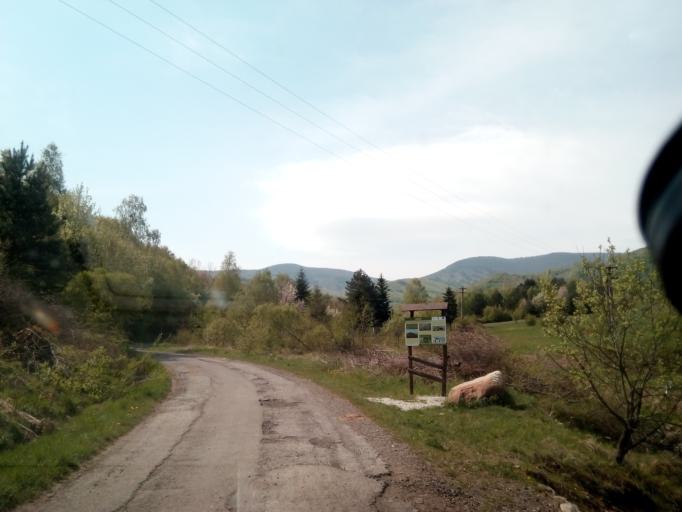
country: SK
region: Presovsky
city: Giraltovce
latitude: 48.9754
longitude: 21.5061
